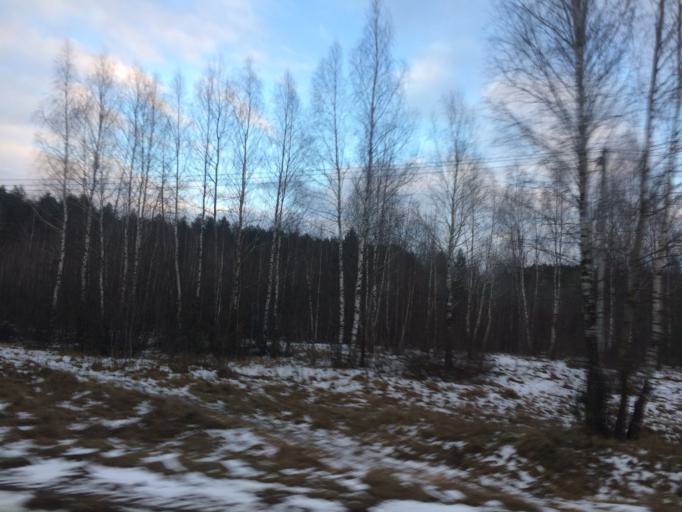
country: RU
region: Tula
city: Cherepet'
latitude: 54.1170
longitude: 36.3606
